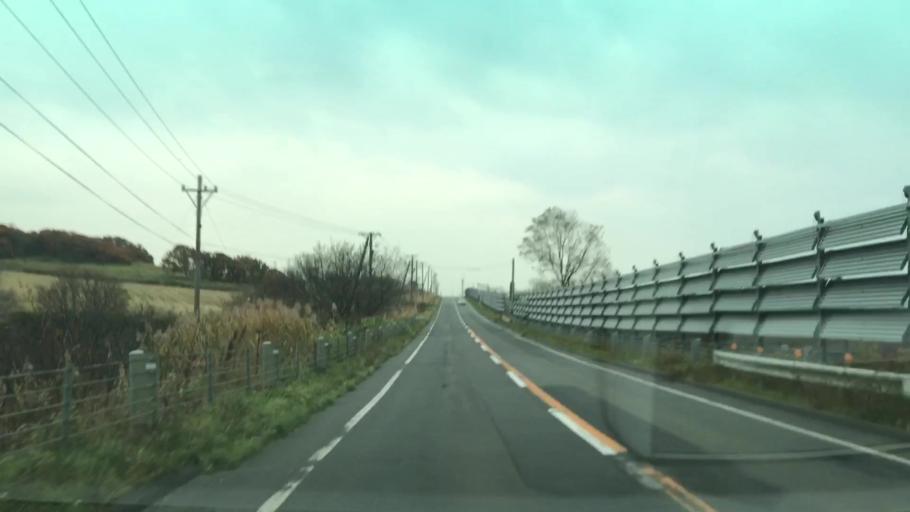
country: JP
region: Hokkaido
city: Ishikari
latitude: 43.3478
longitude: 141.4246
